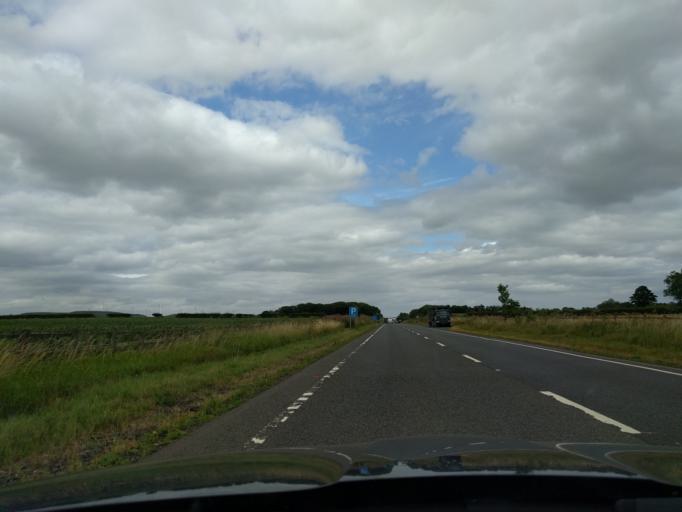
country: GB
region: England
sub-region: Northumberland
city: Ellingham
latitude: 55.4699
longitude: -1.7157
